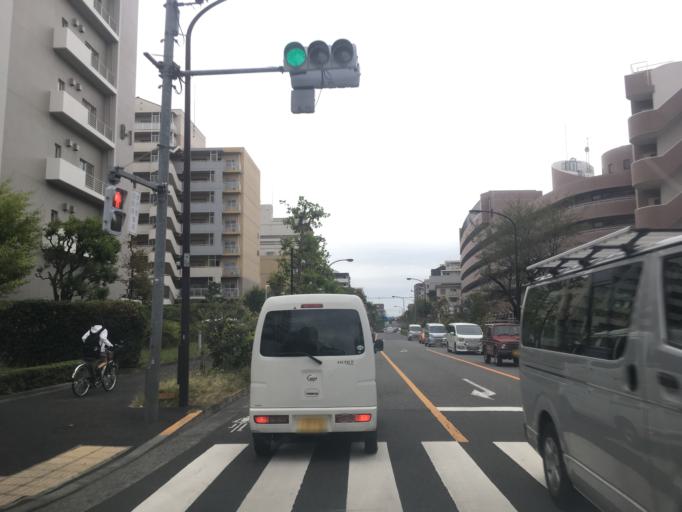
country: JP
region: Tokyo
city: Kokubunji
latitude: 35.6985
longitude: 139.4668
